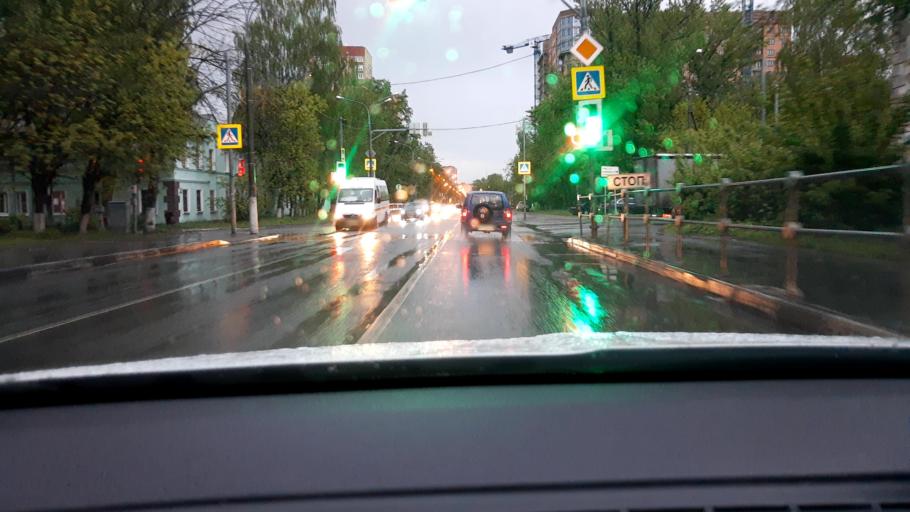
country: RU
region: Moskovskaya
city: Shchelkovo
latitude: 55.9199
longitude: 37.9794
